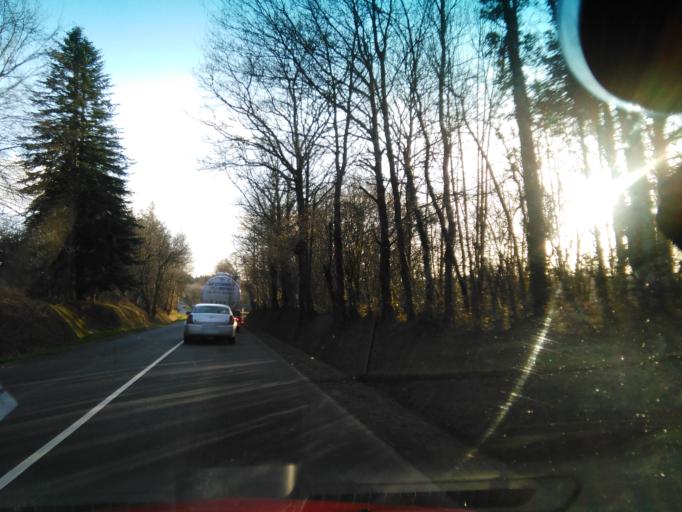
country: FR
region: Lower Normandy
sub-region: Departement de l'Orne
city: Pont-Ecrepin
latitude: 48.6977
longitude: -0.2857
